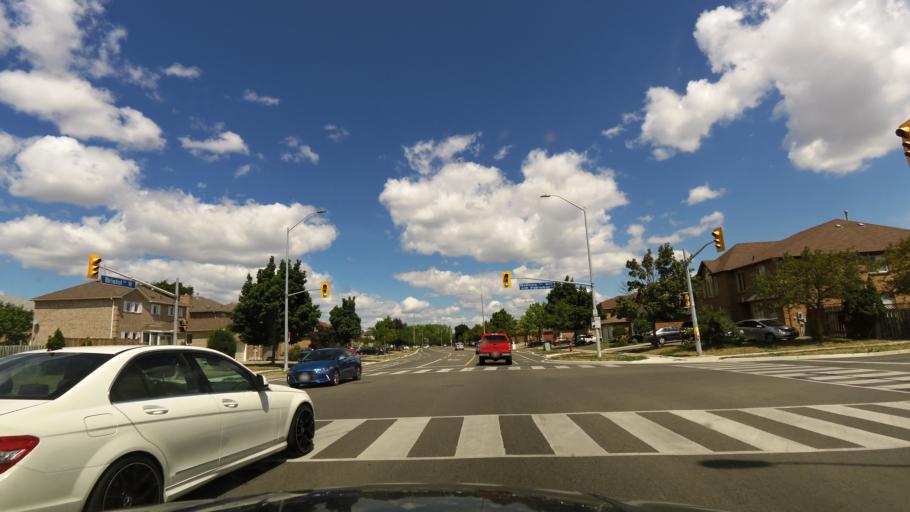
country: CA
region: Ontario
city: Mississauga
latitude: 43.6057
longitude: -79.6695
